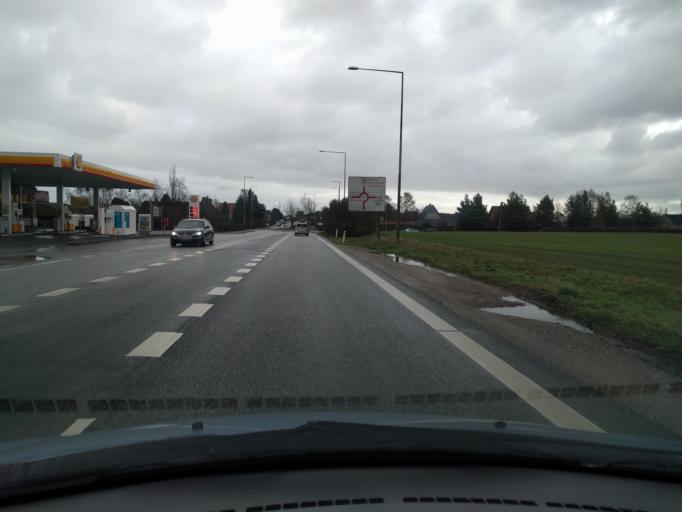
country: DK
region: South Denmark
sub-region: Kerteminde Kommune
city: Langeskov
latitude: 55.3639
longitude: 10.5840
